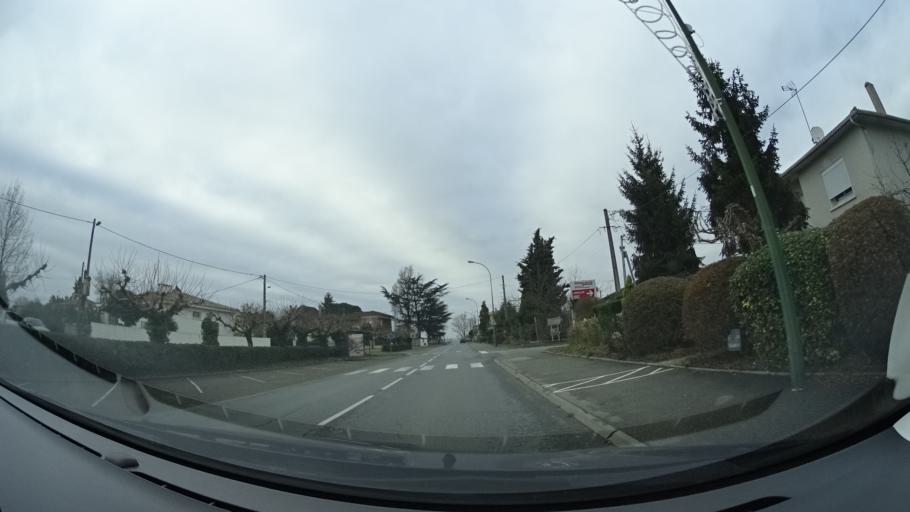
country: FR
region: Aquitaine
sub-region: Departement du Lot-et-Garonne
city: Aiguillon
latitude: 44.2954
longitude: 0.3406
